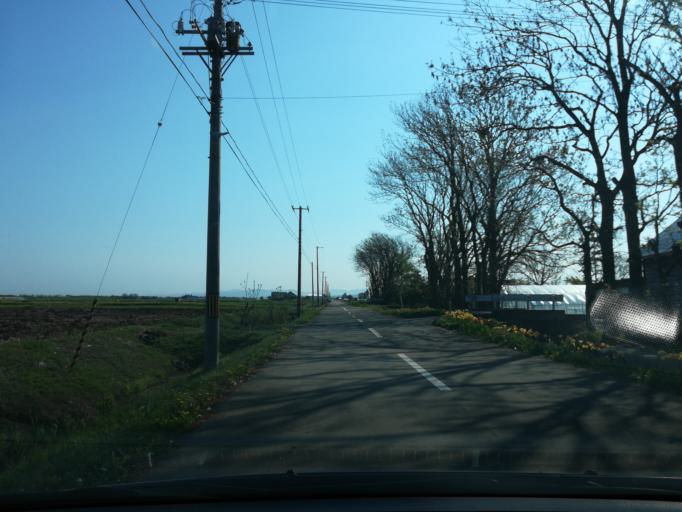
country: JP
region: Hokkaido
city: Iwamizawa
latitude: 43.1381
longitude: 141.6903
